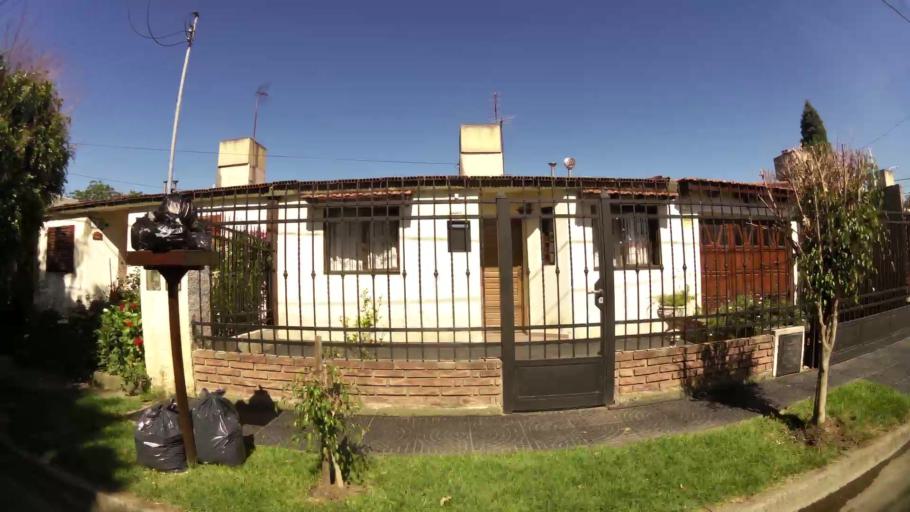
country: AR
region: Cordoba
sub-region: Departamento de Capital
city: Cordoba
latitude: -31.4434
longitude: -64.1385
